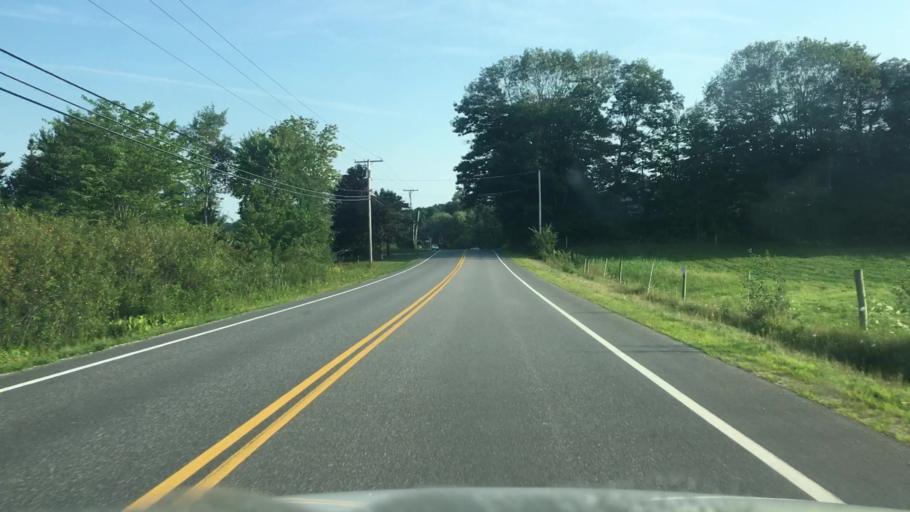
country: US
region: Maine
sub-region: Cumberland County
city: Freeport
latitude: 43.8966
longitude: -70.0946
